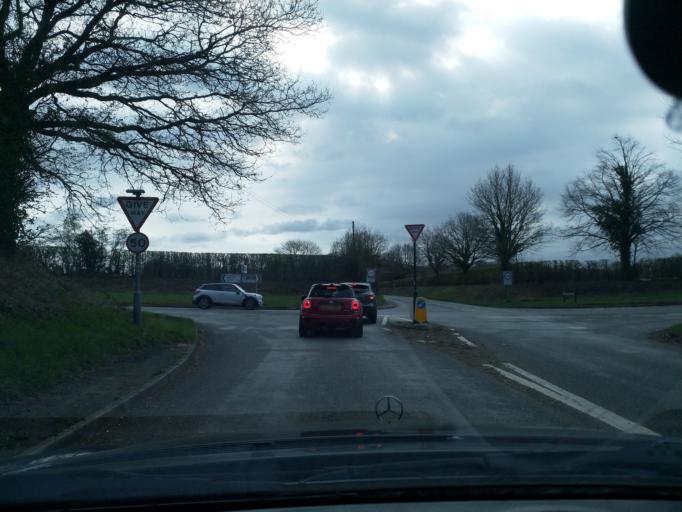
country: GB
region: England
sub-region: Coventry
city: Coventry
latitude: 52.3550
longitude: -1.5235
